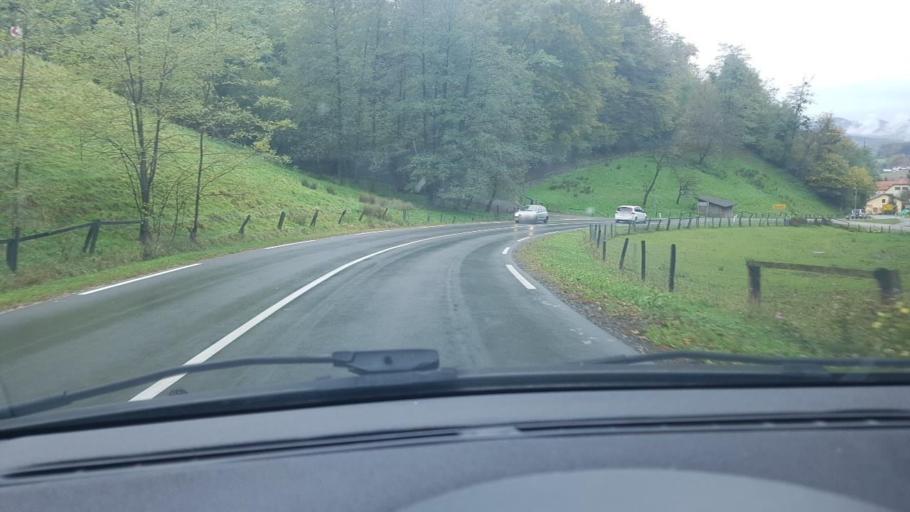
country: SI
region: Majsperk
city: Majsperk
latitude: 46.3530
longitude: 15.7373
